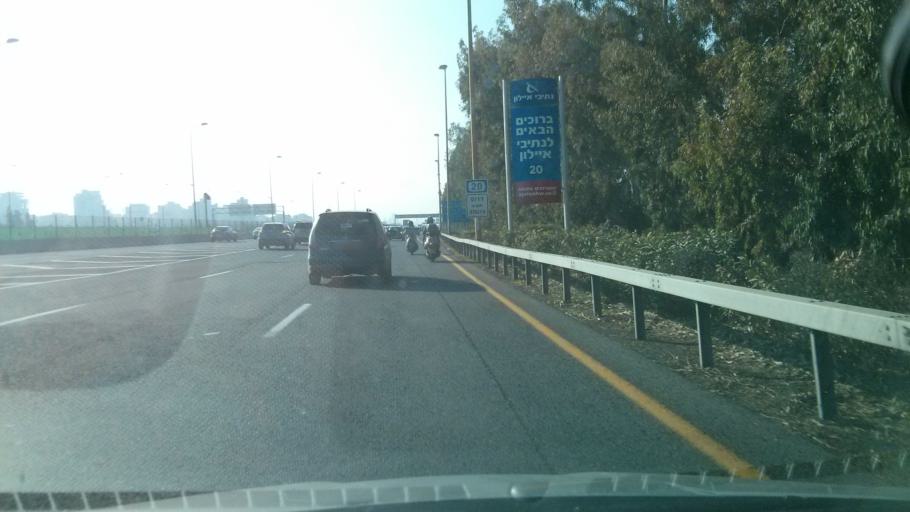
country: IL
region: Tel Aviv
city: Ramat HaSharon
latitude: 32.1353
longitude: 34.8095
